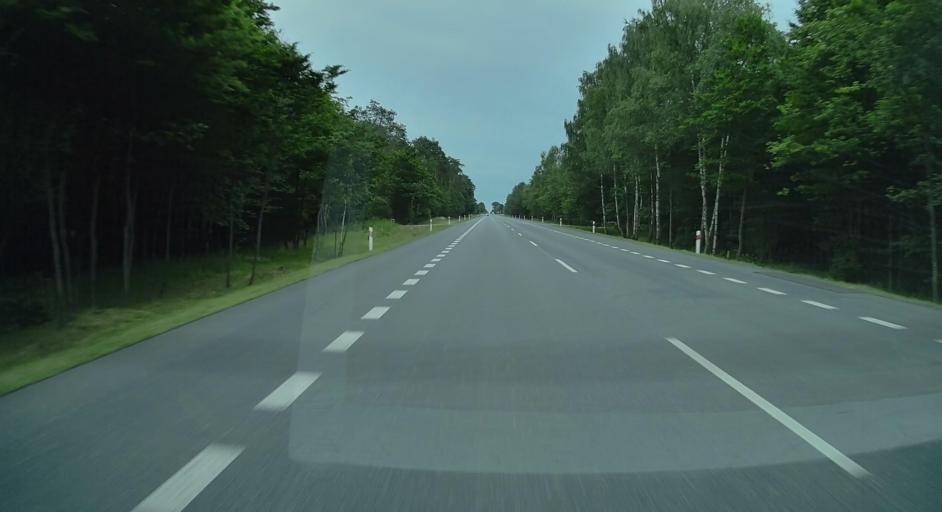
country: PL
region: Lublin Voivodeship
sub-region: Powiat bialski
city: Zalesie
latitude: 52.0345
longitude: 23.2958
